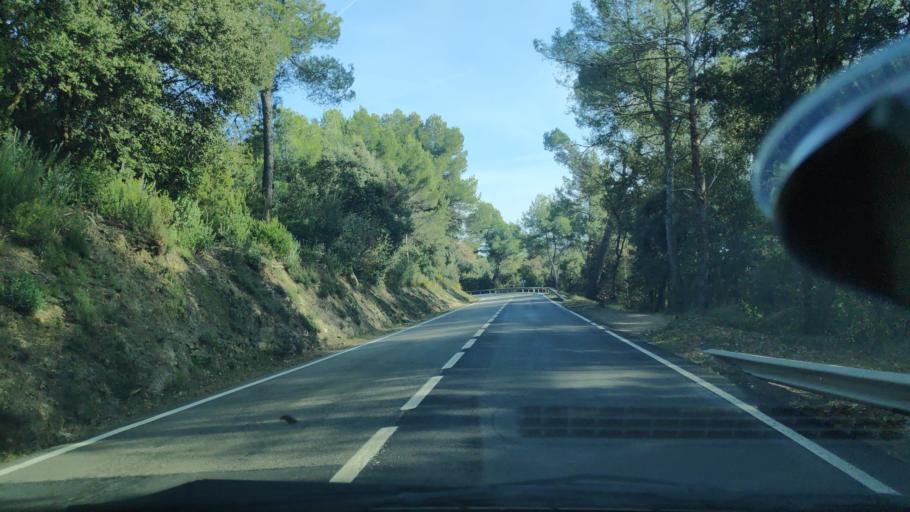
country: ES
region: Catalonia
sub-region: Provincia de Barcelona
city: Castellar del Valles
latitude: 41.6026
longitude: 2.0613
